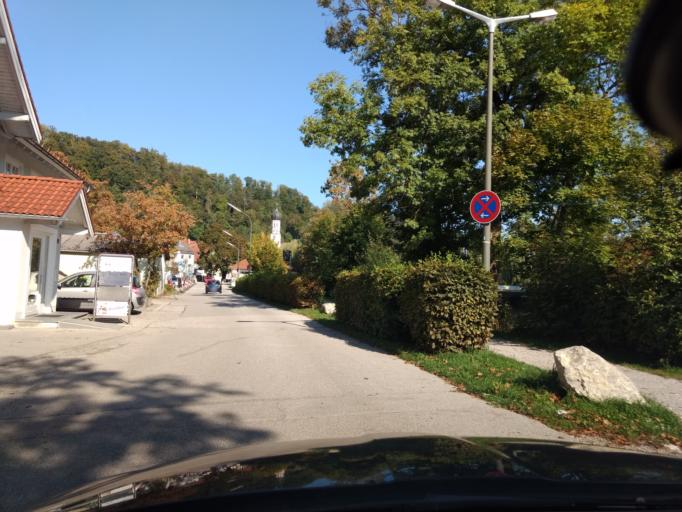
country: DE
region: Bavaria
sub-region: Upper Bavaria
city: Wolfratshausen
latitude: 47.9110
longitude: 11.4194
